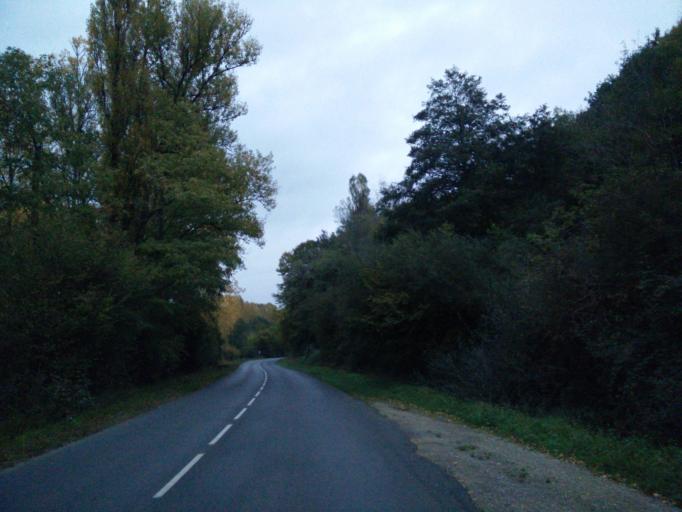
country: FR
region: Aquitaine
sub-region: Departement de la Dordogne
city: Carsac-Aillac
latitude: 44.8534
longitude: 1.2655
